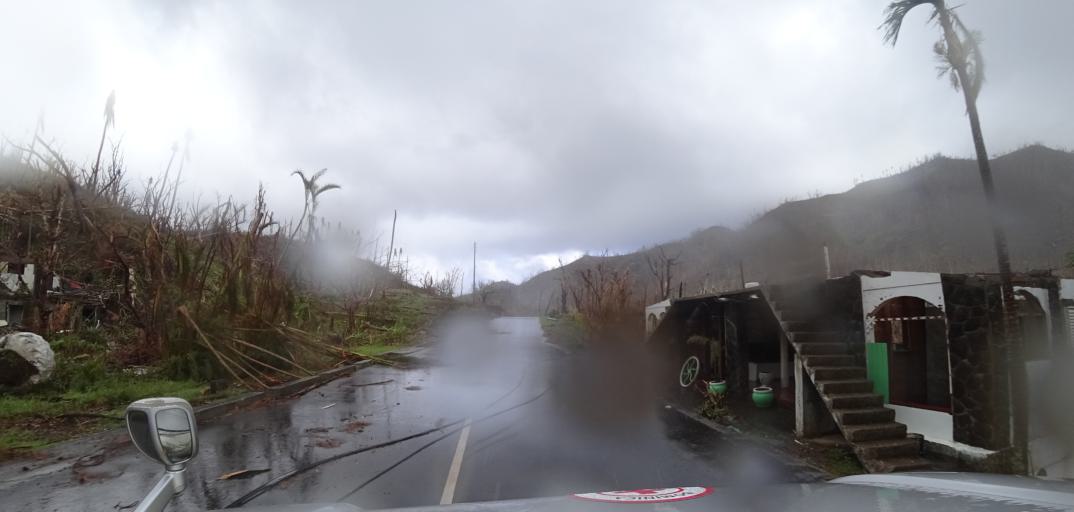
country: DM
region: Saint Andrew
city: Marigot
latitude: 15.4908
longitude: -61.2779
